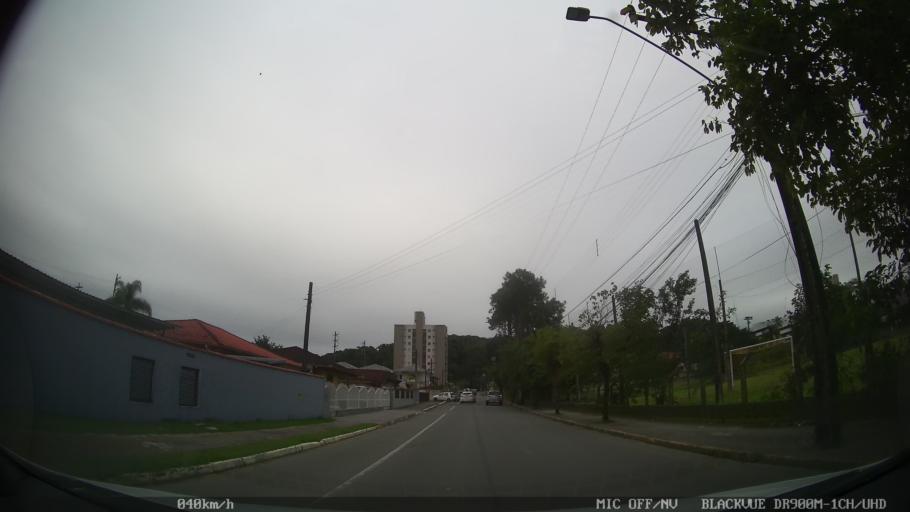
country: BR
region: Santa Catarina
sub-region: Joinville
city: Joinville
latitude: -26.2662
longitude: -48.8487
